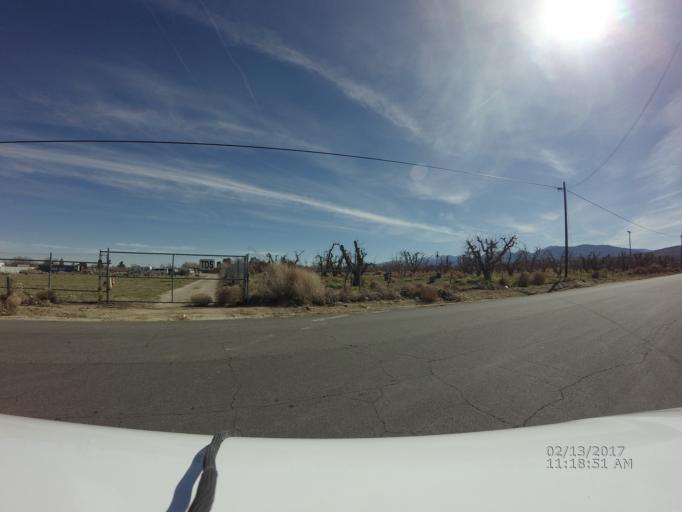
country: US
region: California
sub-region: Los Angeles County
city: Littlerock
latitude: 34.5247
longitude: -117.9925
